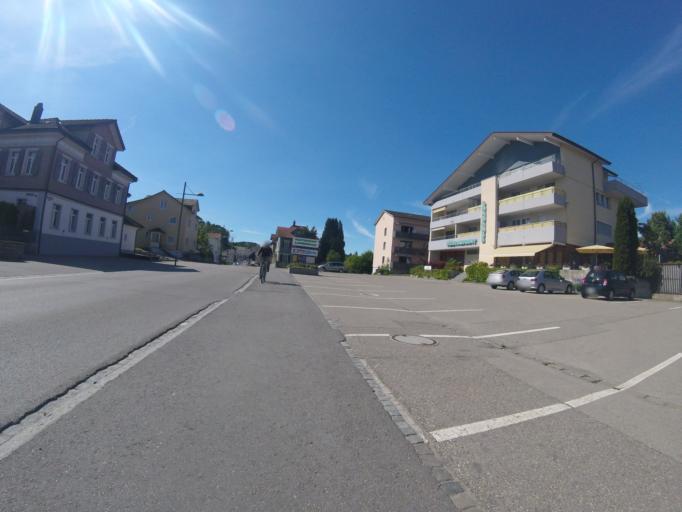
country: CH
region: Saint Gallen
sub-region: Wahlkreis Wil
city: Jonschwil
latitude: 47.4152
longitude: 9.0669
